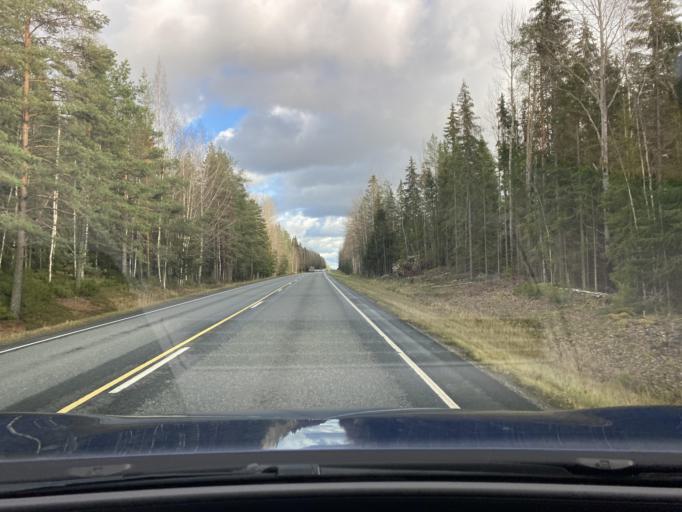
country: FI
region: Haeme
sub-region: Forssa
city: Humppila
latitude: 60.9360
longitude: 23.2613
